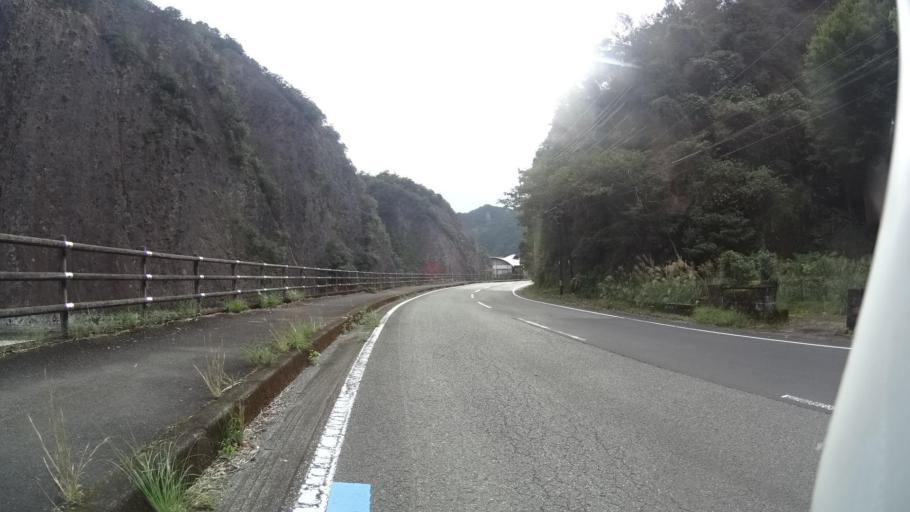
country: JP
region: Wakayama
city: Shingu
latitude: 33.5466
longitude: 135.7190
